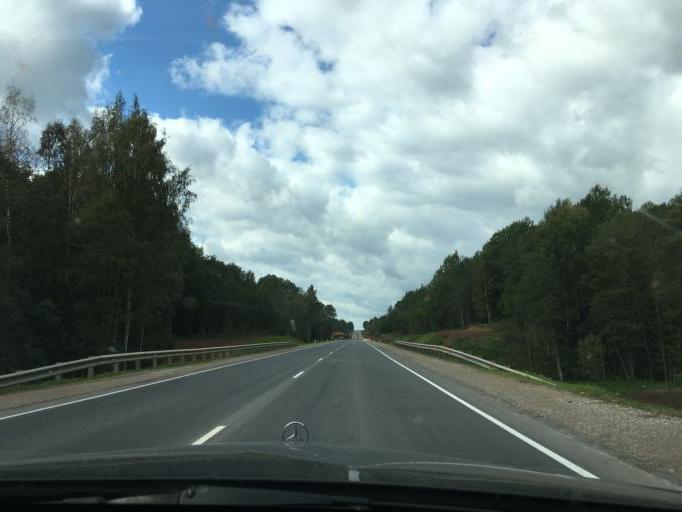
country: RU
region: Tverskaya
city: Toropets
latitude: 56.3107
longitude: 31.1441
